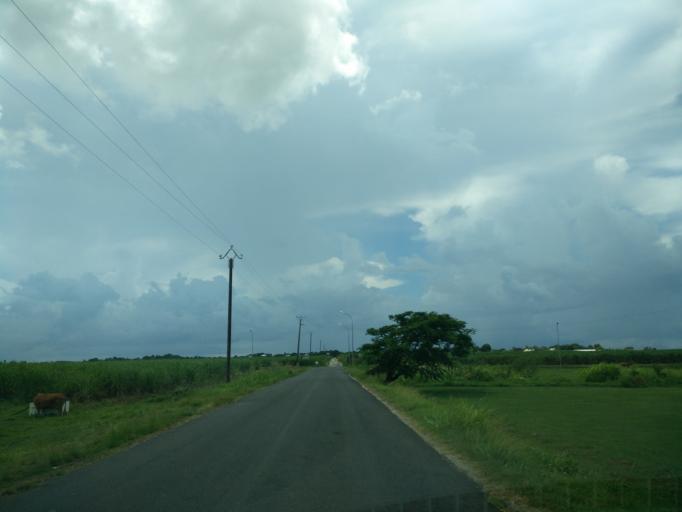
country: GP
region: Guadeloupe
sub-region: Guadeloupe
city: Saint-Francois
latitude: 16.2682
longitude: -61.3301
